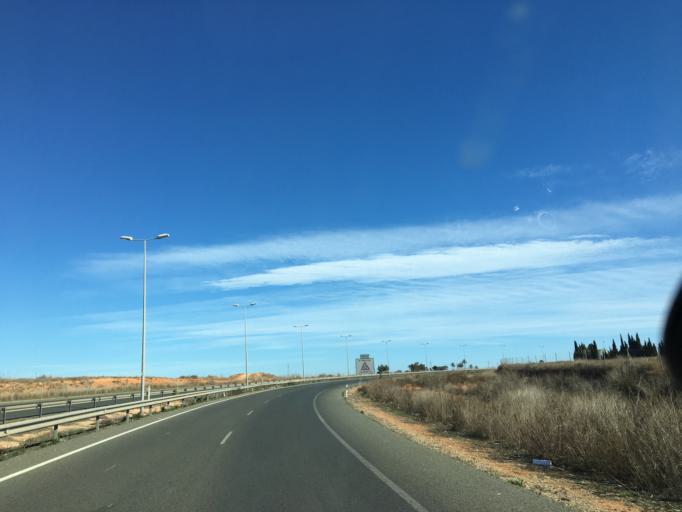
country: ES
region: Murcia
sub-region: Murcia
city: Cartagena
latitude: 37.6385
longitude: -0.9947
